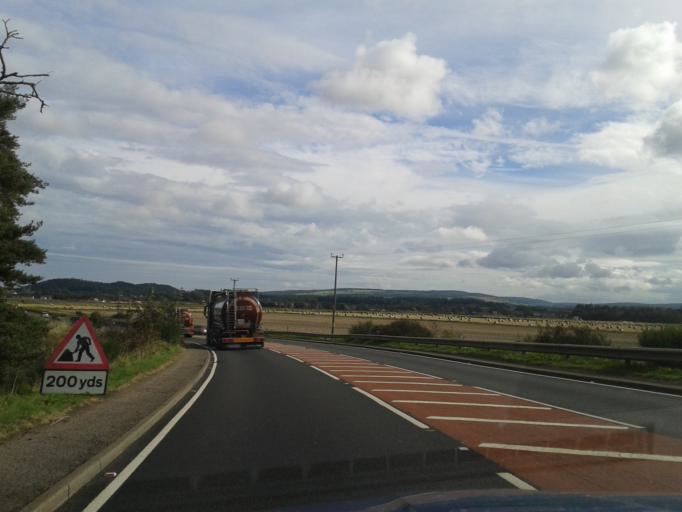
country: GB
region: Scotland
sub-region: Moray
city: Forres
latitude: 57.6018
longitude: -3.6528
